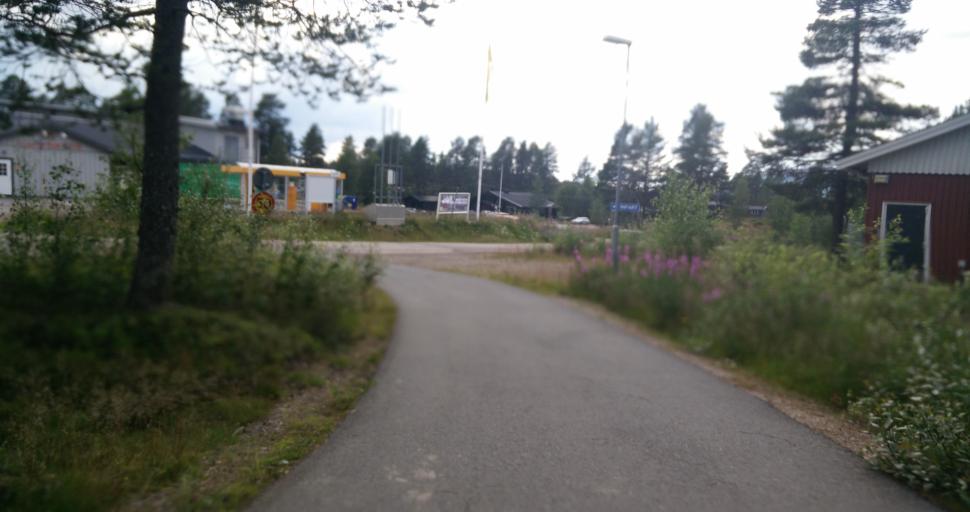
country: NO
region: Hedmark
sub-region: Trysil
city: Innbygda
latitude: 61.1800
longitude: 12.9920
